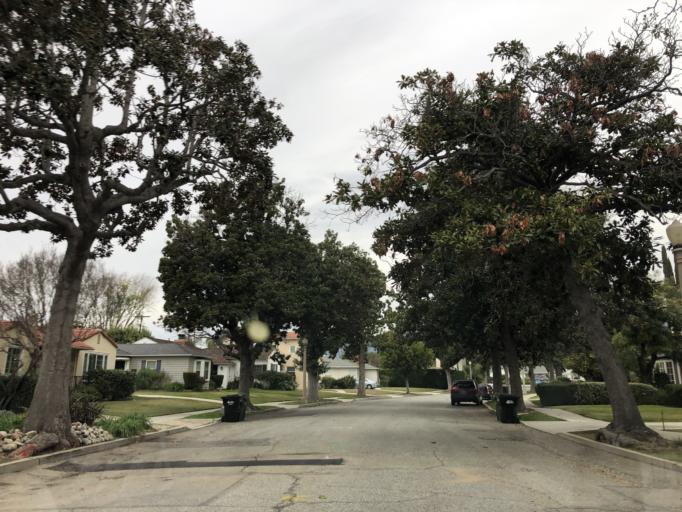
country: US
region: California
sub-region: Los Angeles County
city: San Gabriel
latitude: 34.1084
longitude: -118.1052
